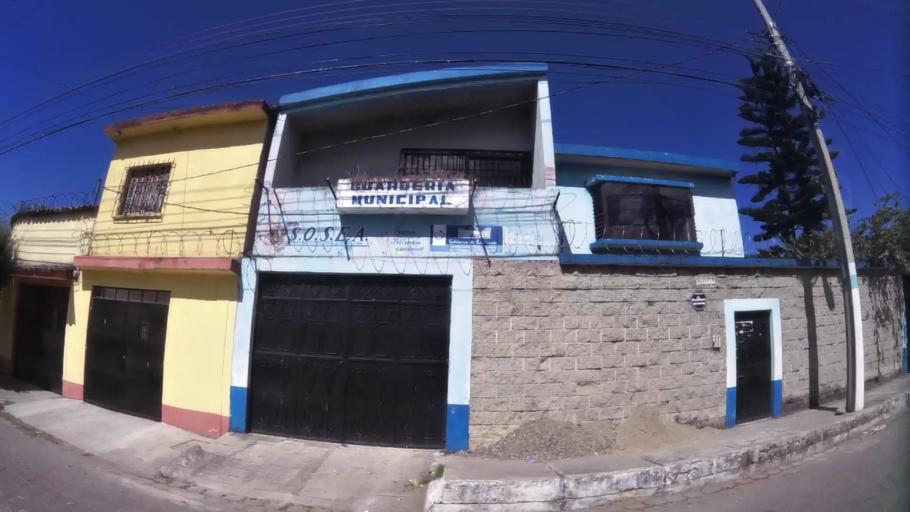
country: GT
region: Guatemala
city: Villa Canales
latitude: 14.4765
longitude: -90.5337
